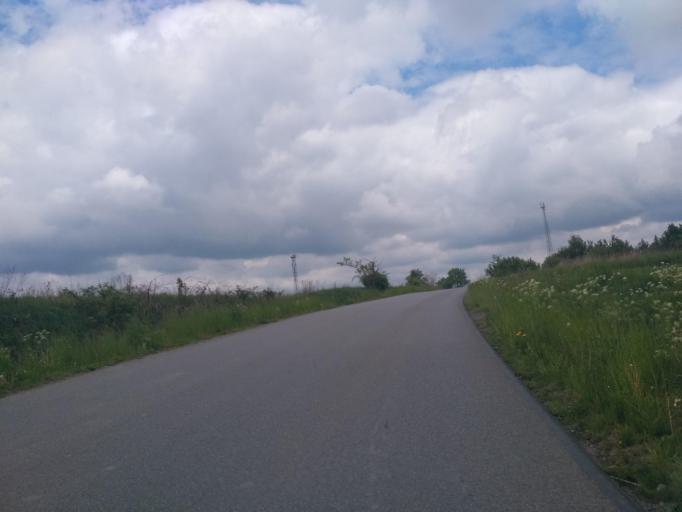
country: PL
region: Subcarpathian Voivodeship
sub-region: Powiat jasielski
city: Tarnowiec
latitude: 49.6671
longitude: 21.6010
